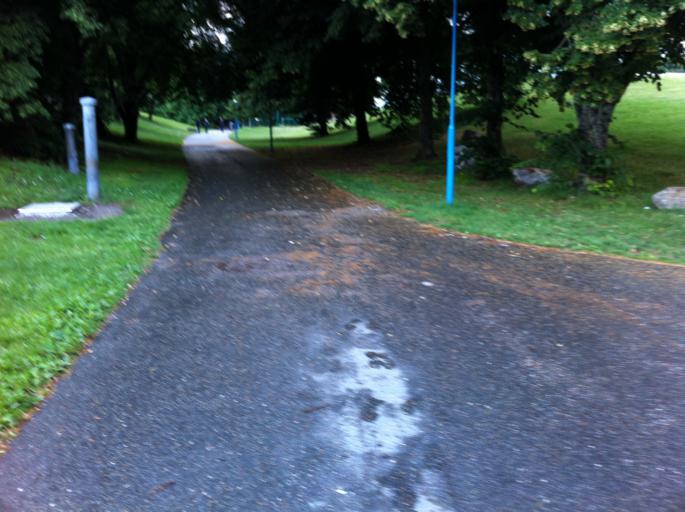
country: SE
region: Stockholm
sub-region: Stockholms Kommun
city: Kista
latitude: 59.3872
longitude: 17.9310
